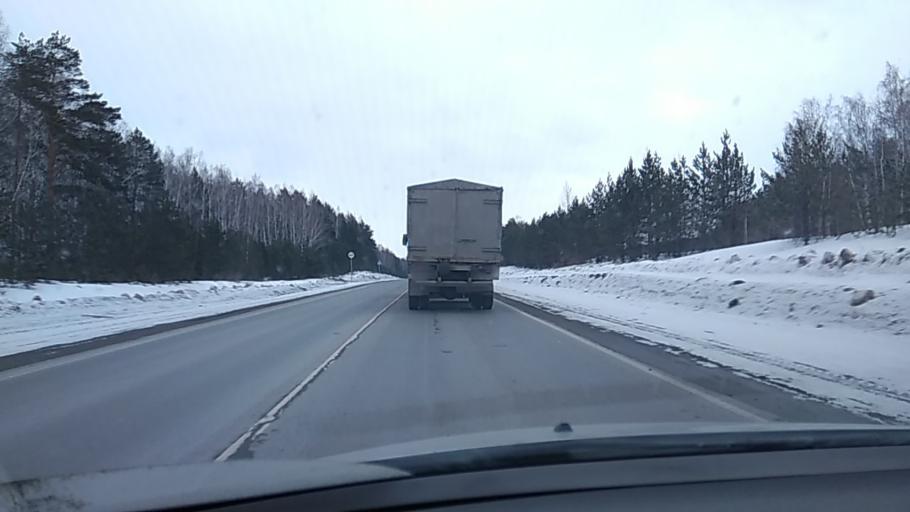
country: RU
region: Sverdlovsk
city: Verkhneye Dubrovo
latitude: 56.7152
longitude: 61.0582
